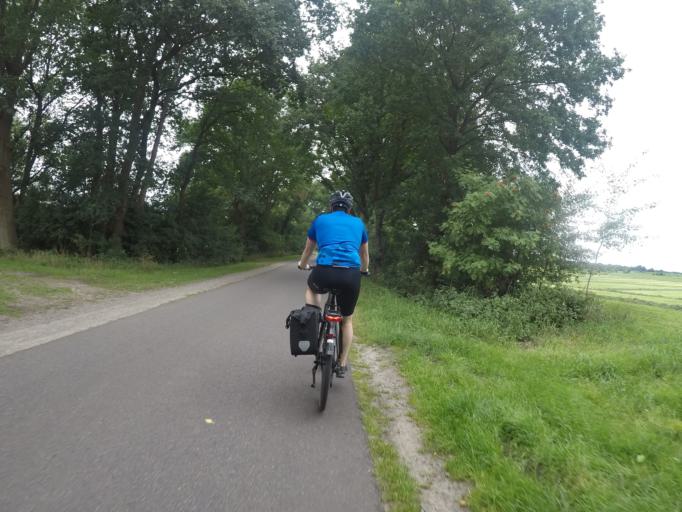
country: DE
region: Lower Saxony
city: Dudenbuttel
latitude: 53.6050
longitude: 9.3405
